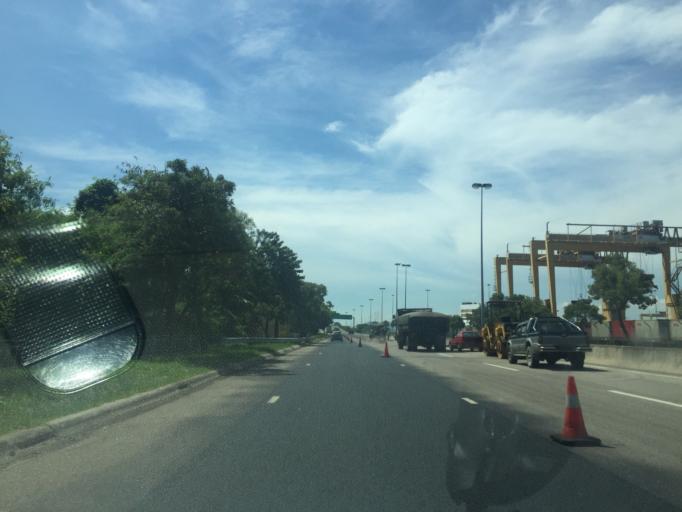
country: MY
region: Penang
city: Butterworth
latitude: 5.4134
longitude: 100.3703
